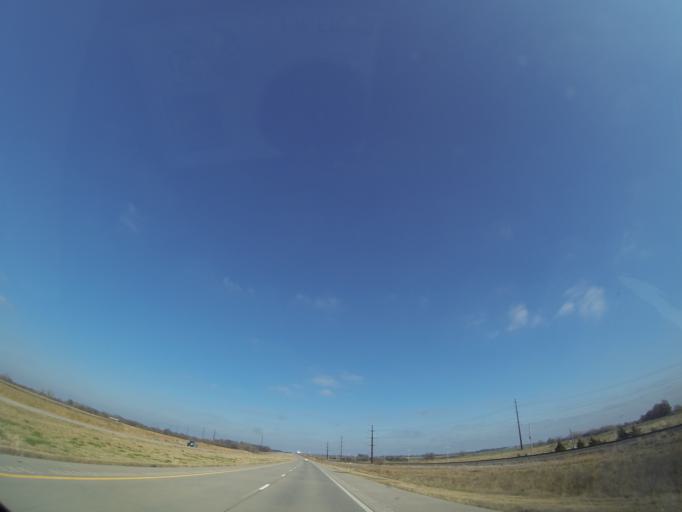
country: US
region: Kansas
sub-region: McPherson County
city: Inman
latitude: 38.1956
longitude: -97.8059
